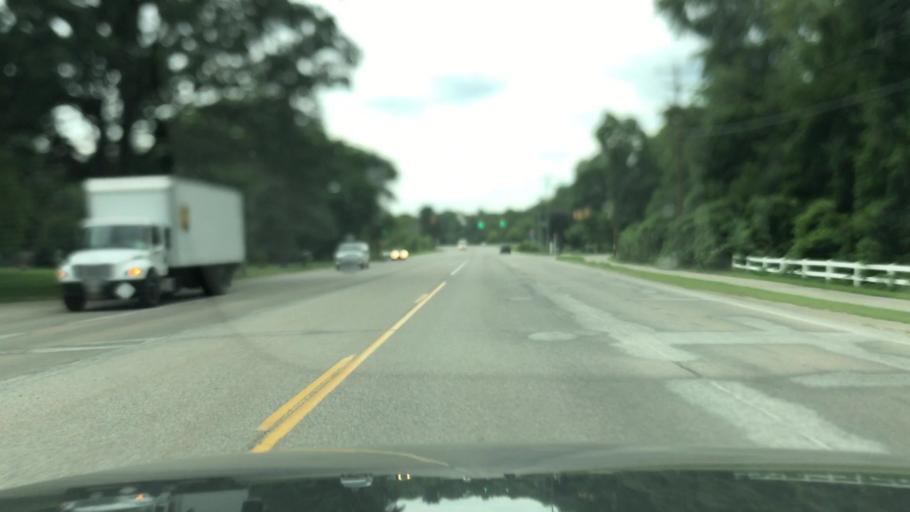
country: US
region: Michigan
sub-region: Kent County
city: Forest Hills
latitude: 42.9195
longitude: -85.5041
